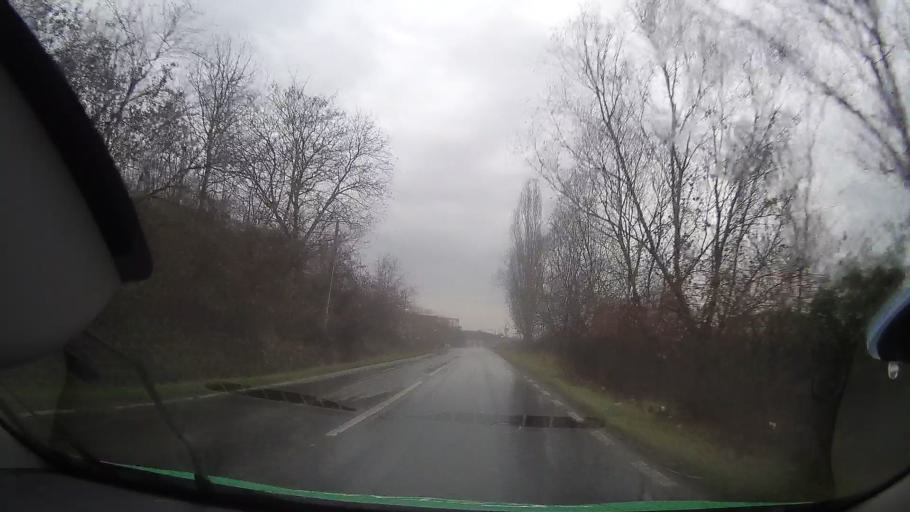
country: RO
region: Bihor
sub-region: Comuna Rabagani
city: Rabagani
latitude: 46.7526
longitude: 22.2096
